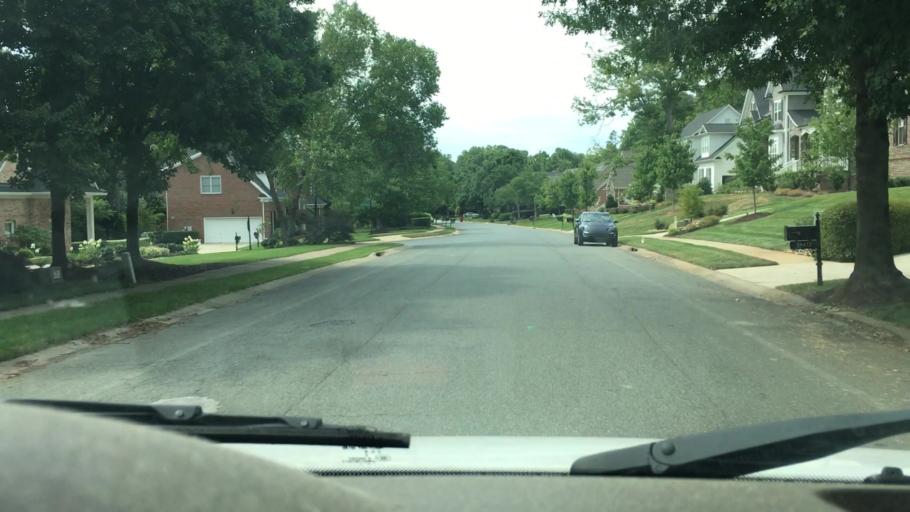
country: US
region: North Carolina
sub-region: Gaston County
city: Davidson
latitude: 35.4691
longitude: -80.7841
